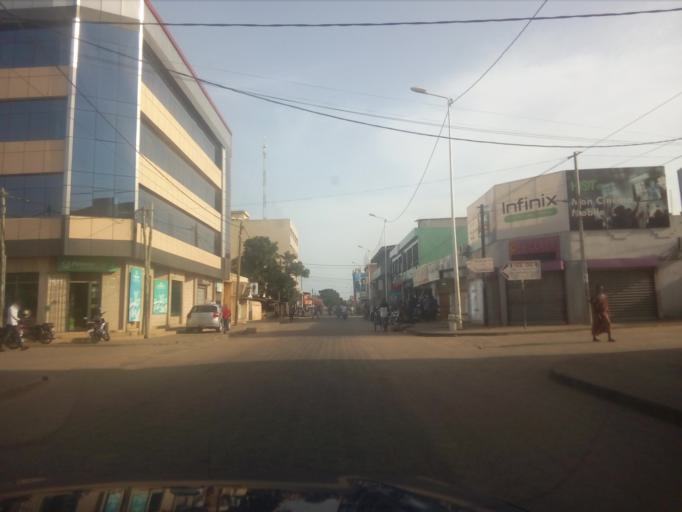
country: TG
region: Maritime
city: Lome
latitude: 6.1377
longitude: 1.2279
